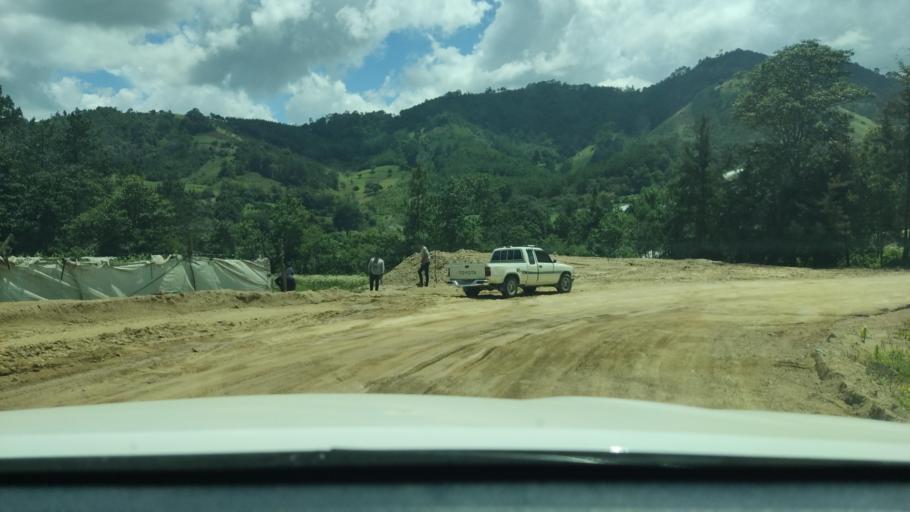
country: GT
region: Chimaltenango
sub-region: Municipio de San Juan Comalapa
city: Comalapa
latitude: 14.7643
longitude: -90.8824
